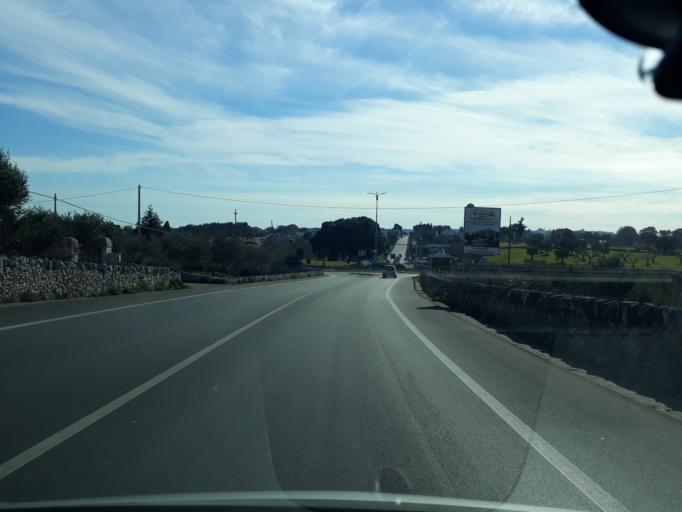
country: IT
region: Apulia
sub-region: Provincia di Bari
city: Locorotondo
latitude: 40.7502
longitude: 17.3290
